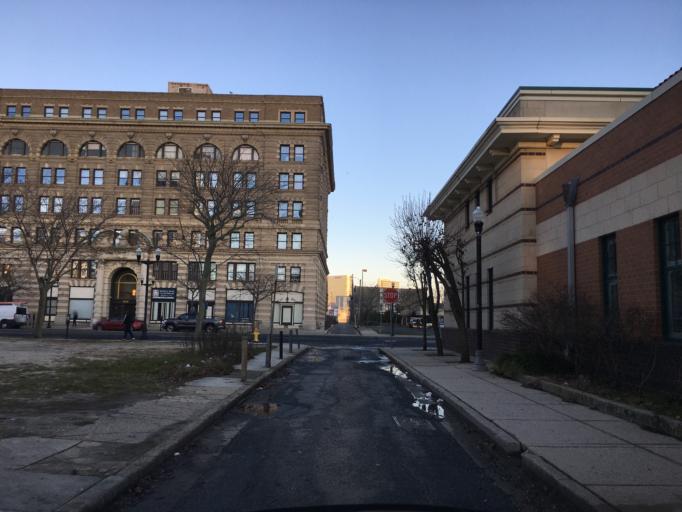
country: US
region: New Jersey
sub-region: Atlantic County
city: Atlantic City
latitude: 39.3631
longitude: -74.4247
